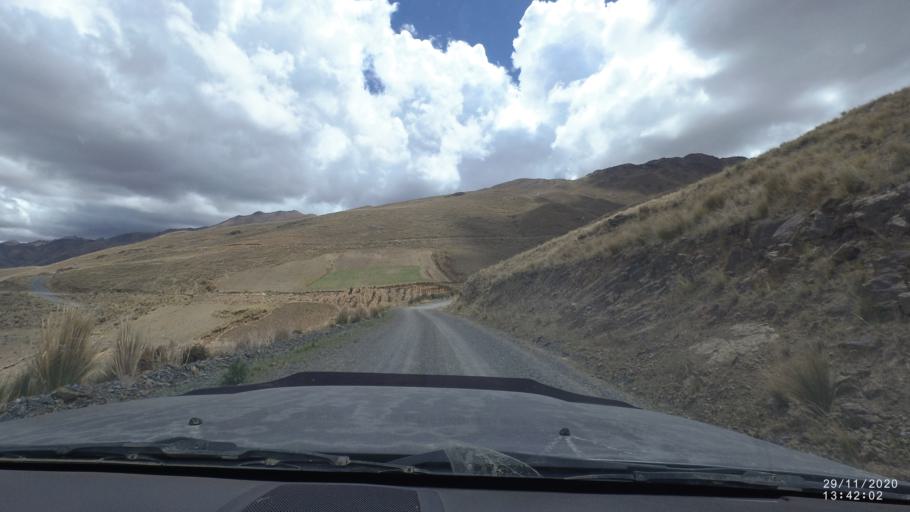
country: BO
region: Cochabamba
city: Cochabamba
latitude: -17.1346
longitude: -66.3234
